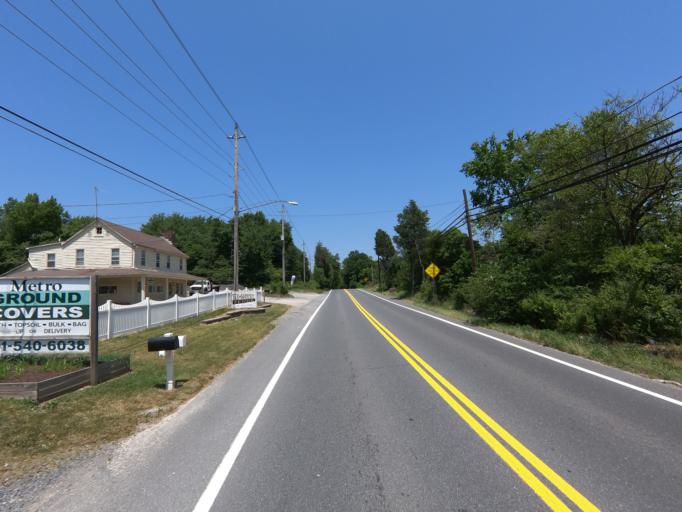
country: US
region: Maryland
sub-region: Montgomery County
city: Clarksburg
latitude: 39.2586
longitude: -77.3026
